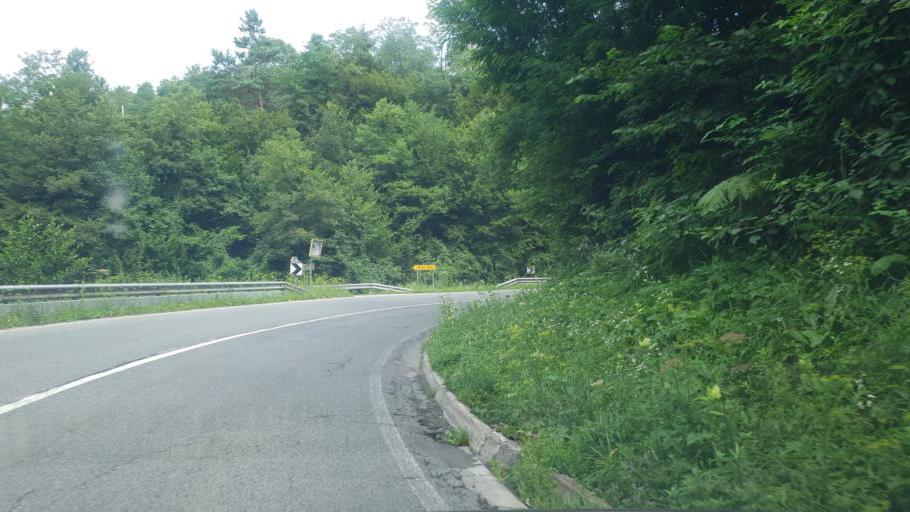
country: SI
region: Ilirska Bistrica
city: Ilirska Bistrica
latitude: 45.5228
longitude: 14.2467
